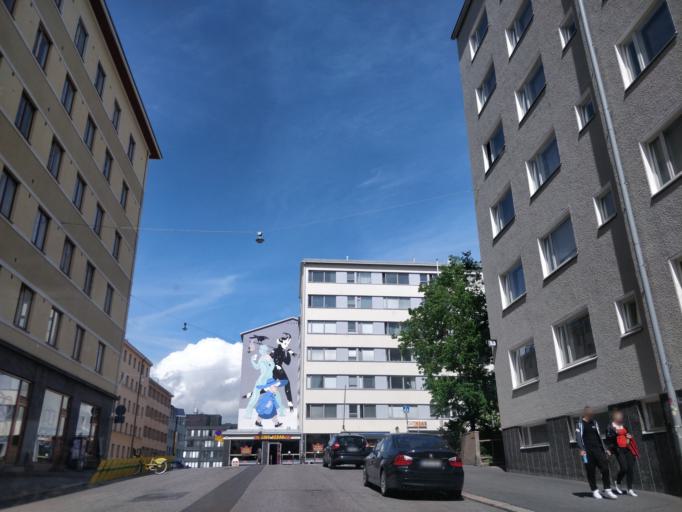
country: FI
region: Uusimaa
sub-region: Helsinki
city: Helsinki
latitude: 60.1879
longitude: 24.9562
